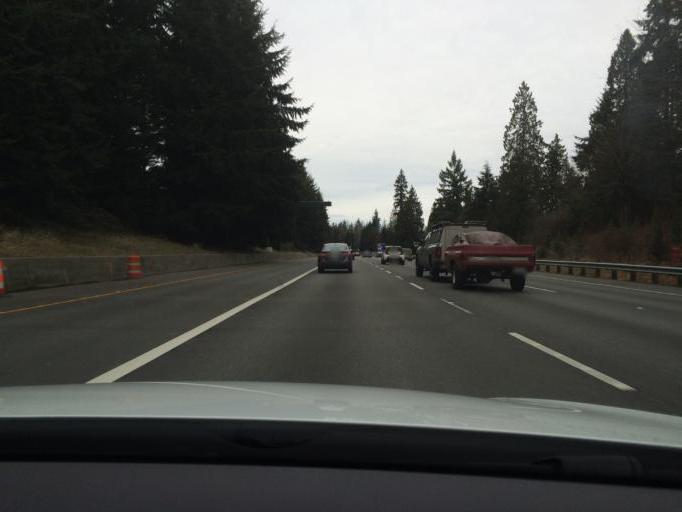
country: US
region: Washington
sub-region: King County
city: Bothell
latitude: 47.7808
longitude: -122.1933
